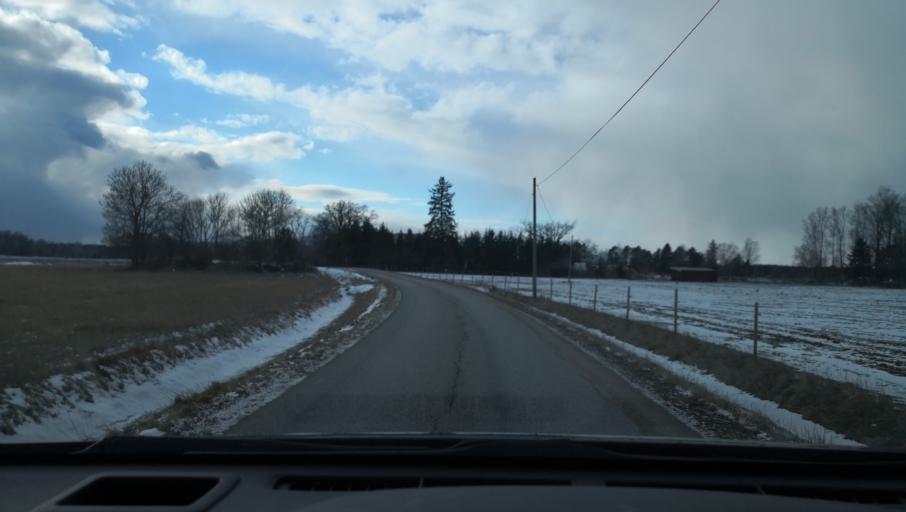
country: SE
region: Uppsala
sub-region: Enkopings Kommun
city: Irsta
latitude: 59.7025
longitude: 16.9356
